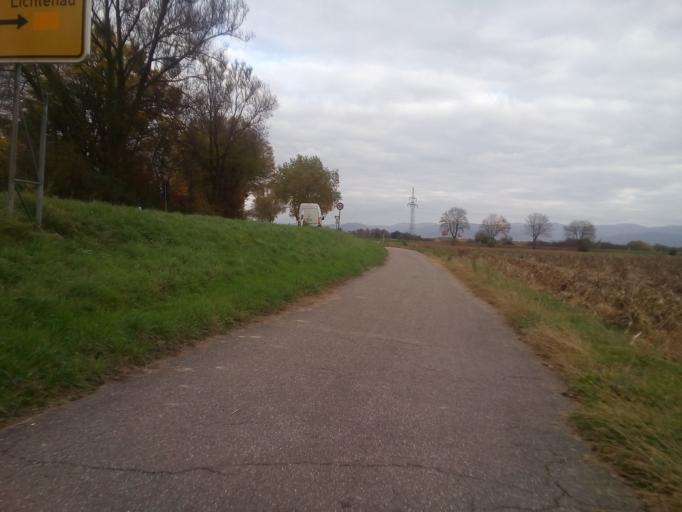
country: DE
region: Baden-Wuerttemberg
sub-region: Karlsruhe Region
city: Rheinmuenster
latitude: 48.7513
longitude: 8.0165
